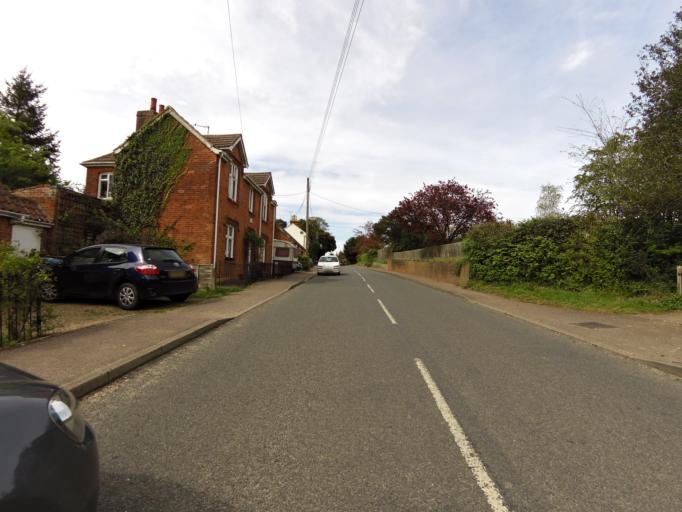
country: GB
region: England
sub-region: Suffolk
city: Ipswich
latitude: 51.9815
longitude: 1.1584
